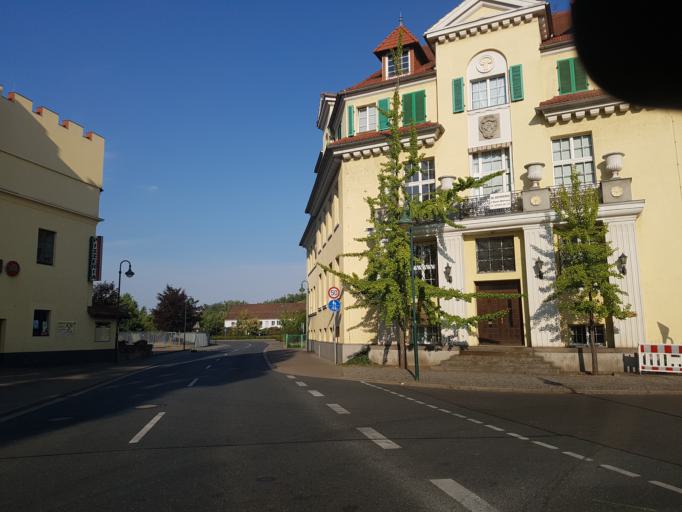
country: DE
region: Saxony
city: Nauwalde
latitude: 51.4092
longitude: 13.4432
